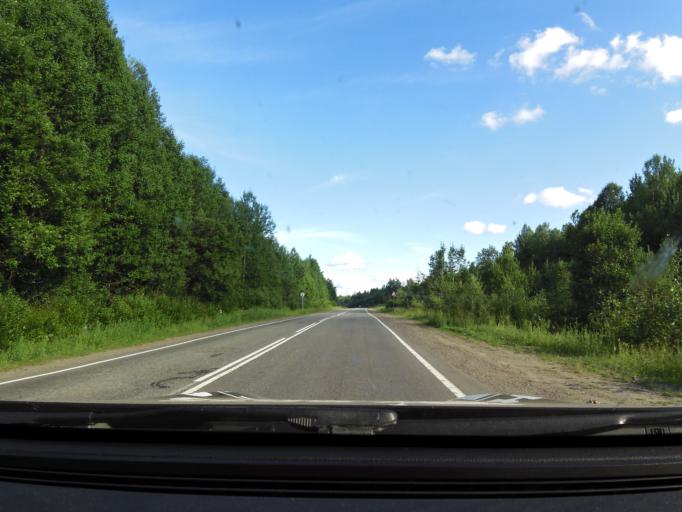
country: RU
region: Kirov
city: Omutninsk
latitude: 58.7109
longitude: 52.0975
